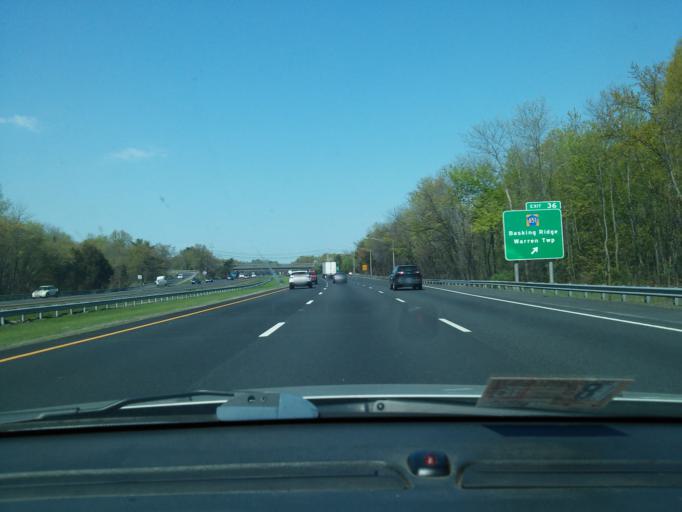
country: US
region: New Jersey
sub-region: Somerset County
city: Warren Township
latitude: 40.6482
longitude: -74.5173
